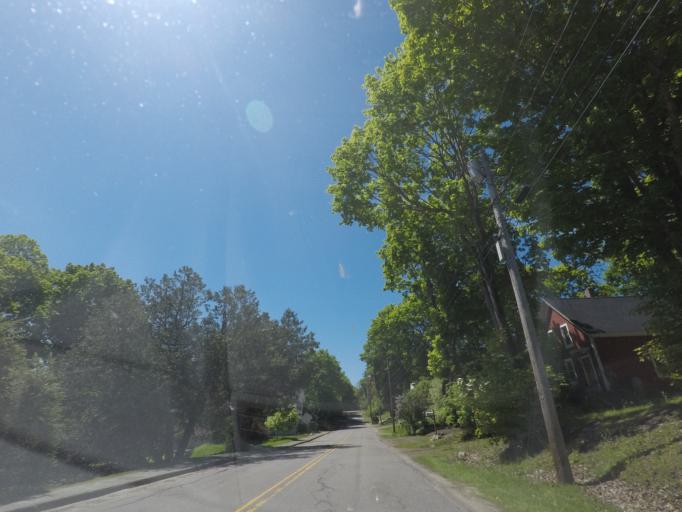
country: US
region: Maine
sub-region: Kennebec County
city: Hallowell
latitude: 44.2815
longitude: -69.7953
